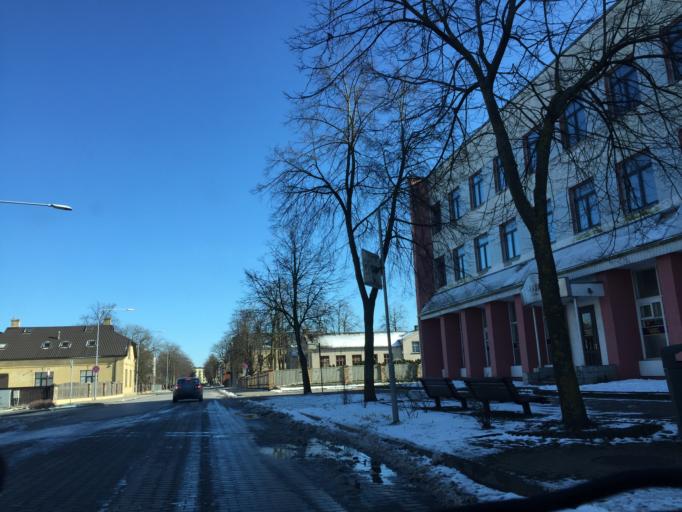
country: LV
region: Ventspils
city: Ventspils
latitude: 57.3915
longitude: 21.5660
